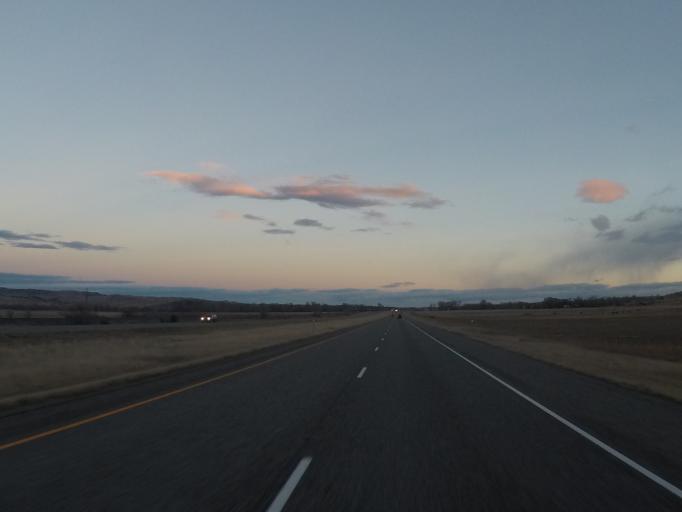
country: US
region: Montana
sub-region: Sweet Grass County
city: Big Timber
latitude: 45.7855
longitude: -109.8170
